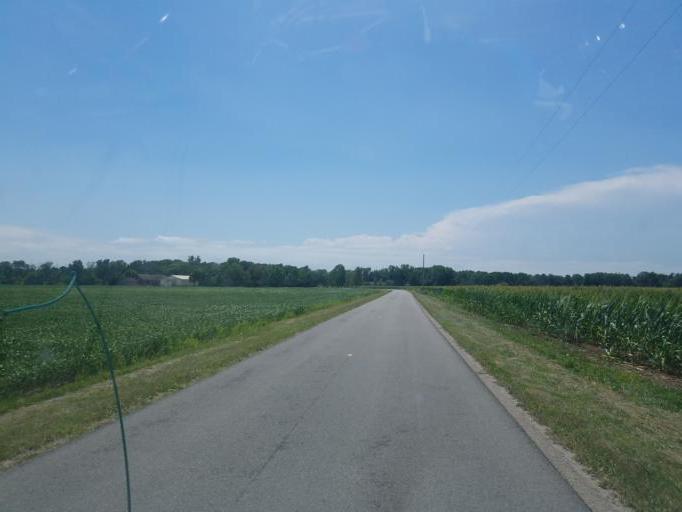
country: US
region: Ohio
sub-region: Paulding County
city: Antwerp
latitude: 41.1860
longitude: -84.7802
